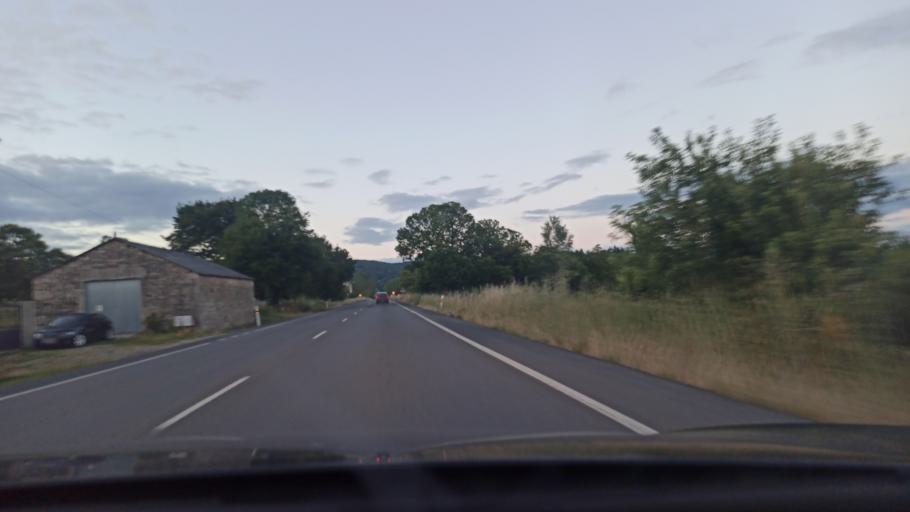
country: ES
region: Galicia
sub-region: Provincia de Lugo
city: Guntin
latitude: 42.9104
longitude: -7.6688
